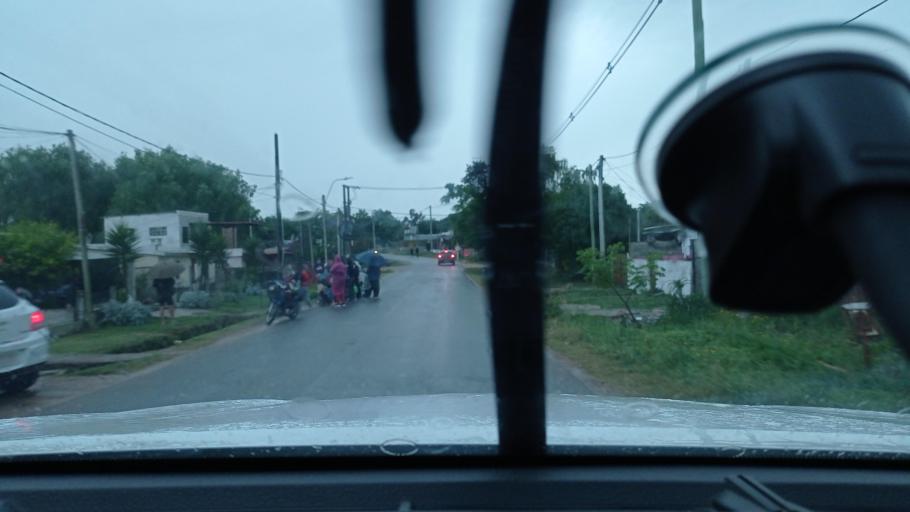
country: UY
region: Canelones
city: Joaquin Suarez
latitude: -34.7545
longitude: -56.0163
